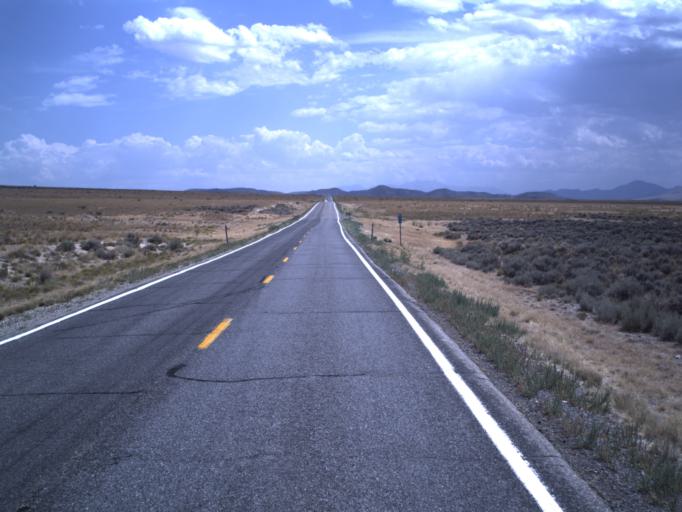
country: US
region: Utah
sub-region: Utah County
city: Eagle Mountain
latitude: 40.2734
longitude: -112.2482
